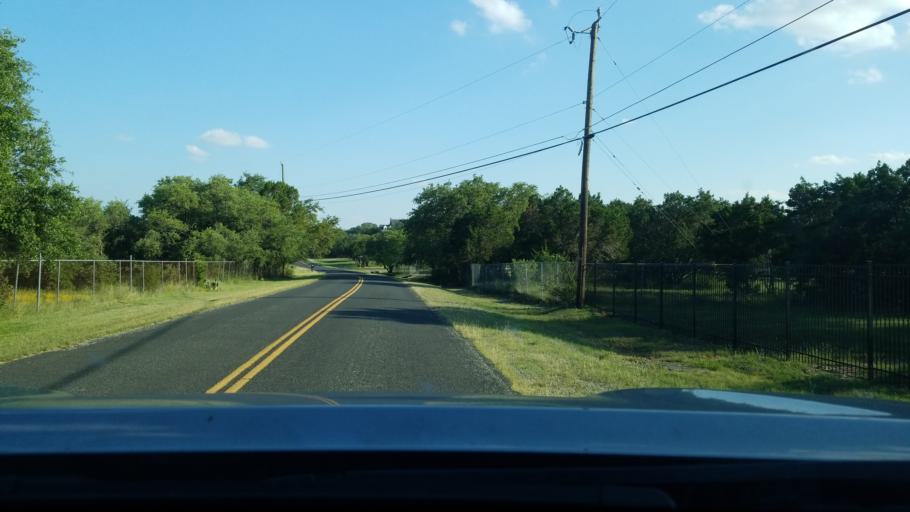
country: US
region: Texas
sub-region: Bexar County
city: Timberwood Park
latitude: 29.7043
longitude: -98.4378
